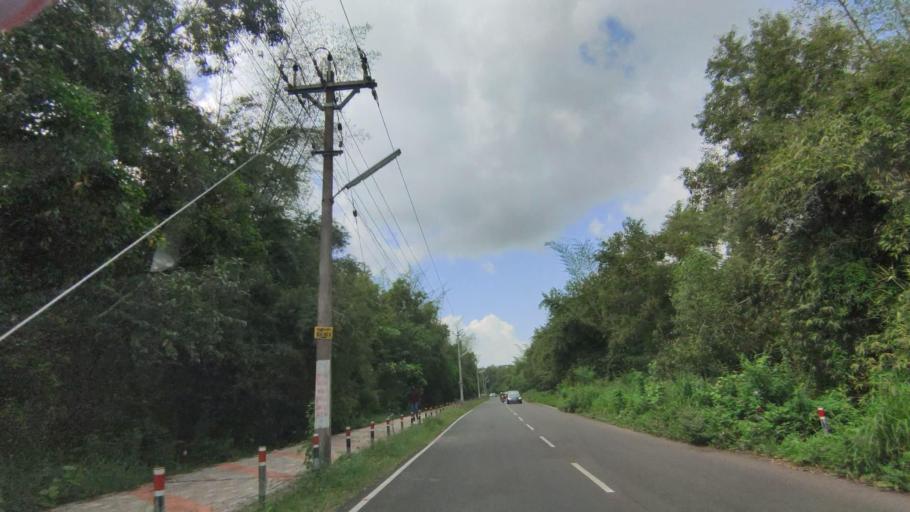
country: IN
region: Kerala
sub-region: Kottayam
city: Kottayam
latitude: 9.5707
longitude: 76.5228
